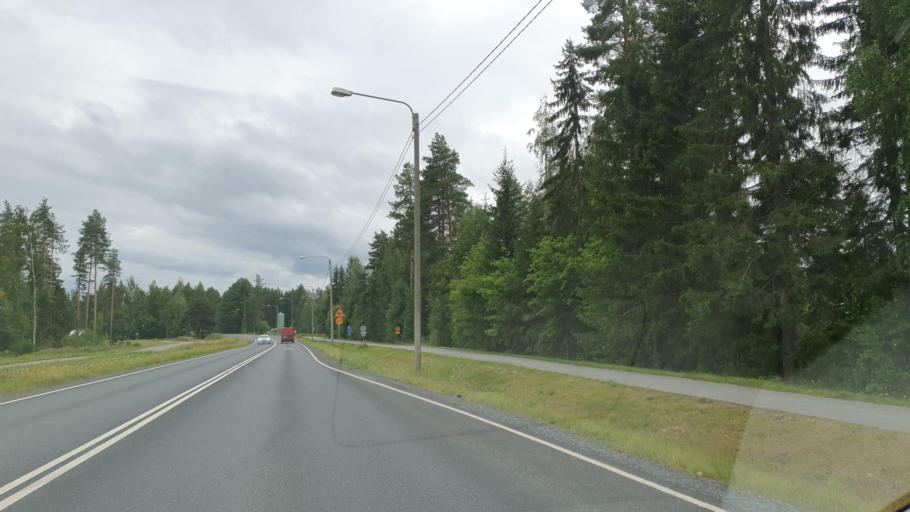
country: FI
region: Northern Savo
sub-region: Ylae-Savo
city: Lapinlahti
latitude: 63.4237
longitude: 27.3302
